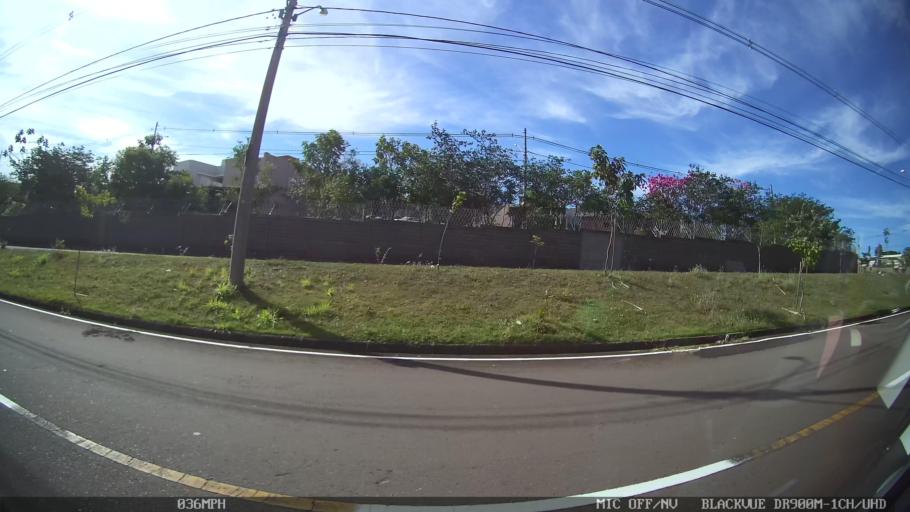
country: BR
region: Sao Paulo
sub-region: Sao Jose Do Rio Preto
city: Sao Jose do Rio Preto
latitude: -20.8110
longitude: -49.3361
